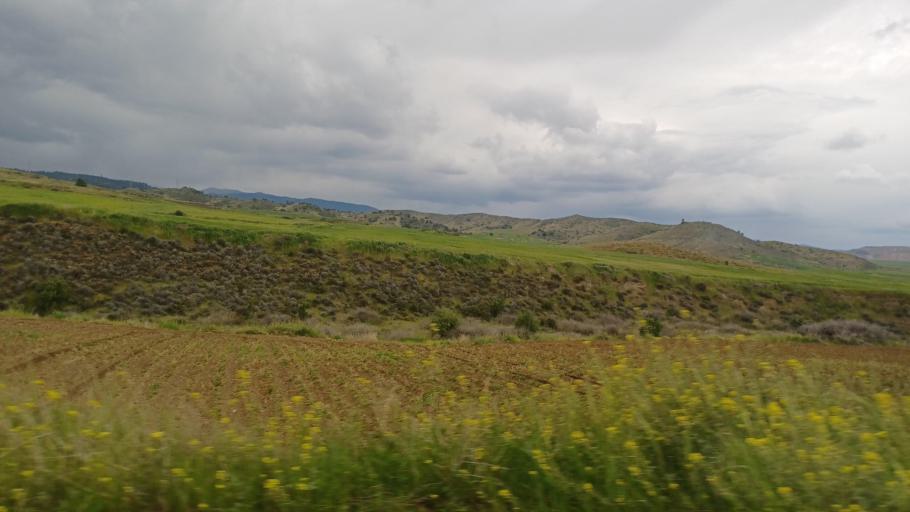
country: CY
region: Lefkosia
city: Astromeritis
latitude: 35.0861
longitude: 32.9530
